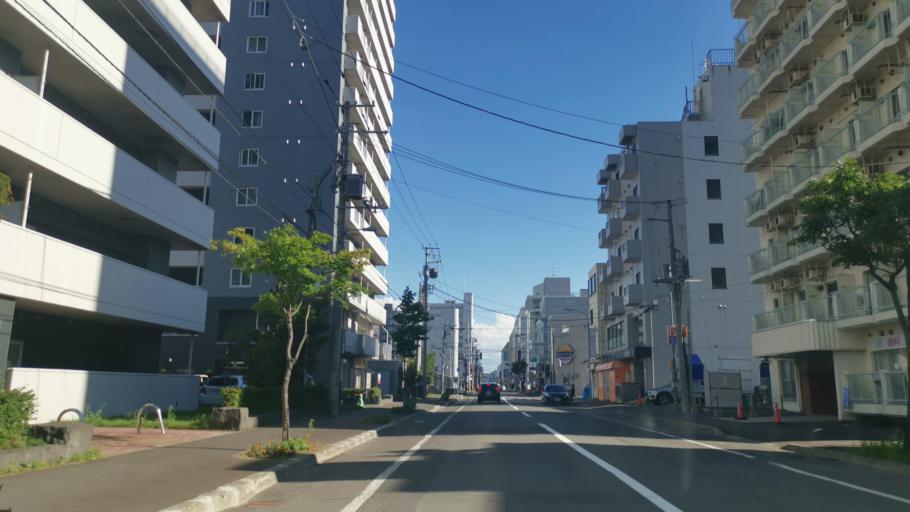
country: JP
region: Hokkaido
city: Sapporo
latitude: 43.0926
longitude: 141.3440
